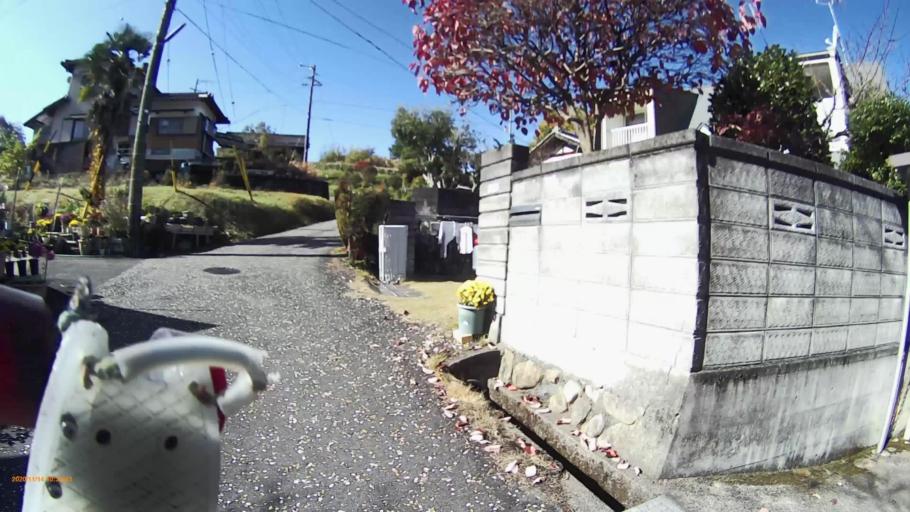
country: JP
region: Gifu
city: Nakatsugawa
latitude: 35.5125
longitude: 137.5291
